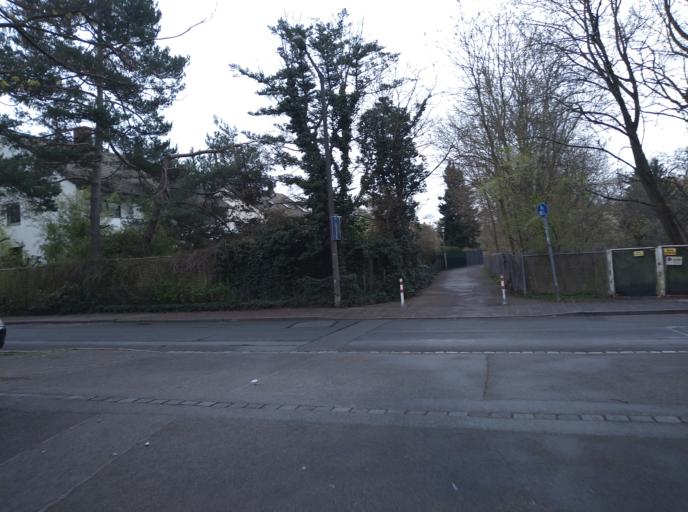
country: DE
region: Bavaria
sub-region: Regierungsbezirk Mittelfranken
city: Nuernberg
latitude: 49.4472
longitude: 11.1131
